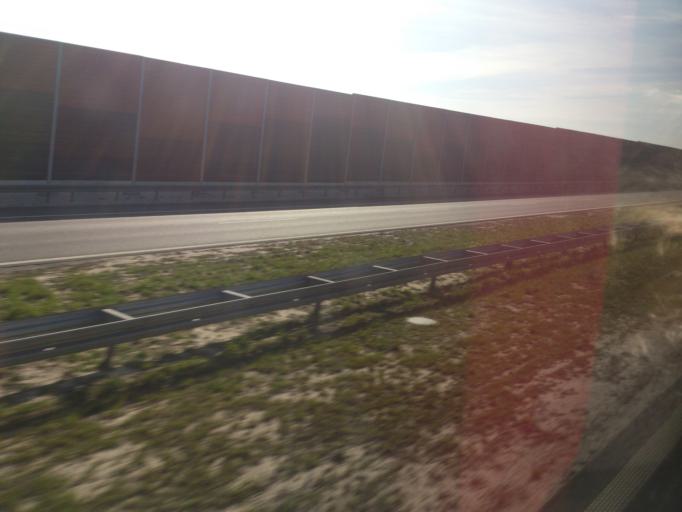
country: PL
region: Kujawsko-Pomorskie
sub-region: Powiat aleksandrowski
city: Waganiec
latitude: 52.7689
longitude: 18.8489
